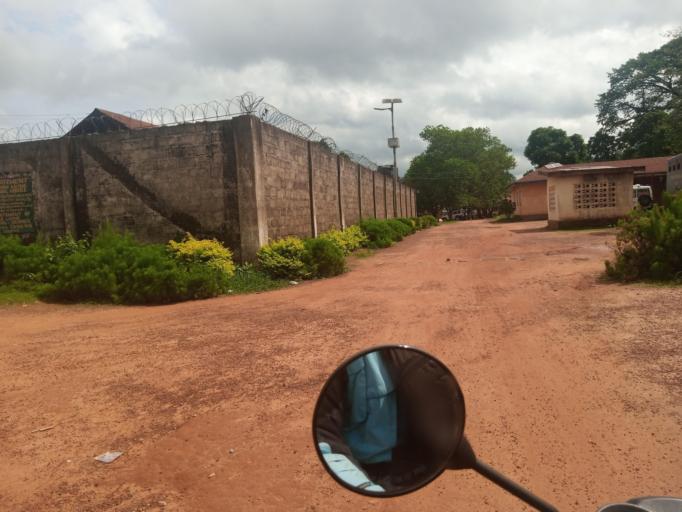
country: SL
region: Southern Province
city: Bo
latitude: 7.9693
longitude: -11.7424
